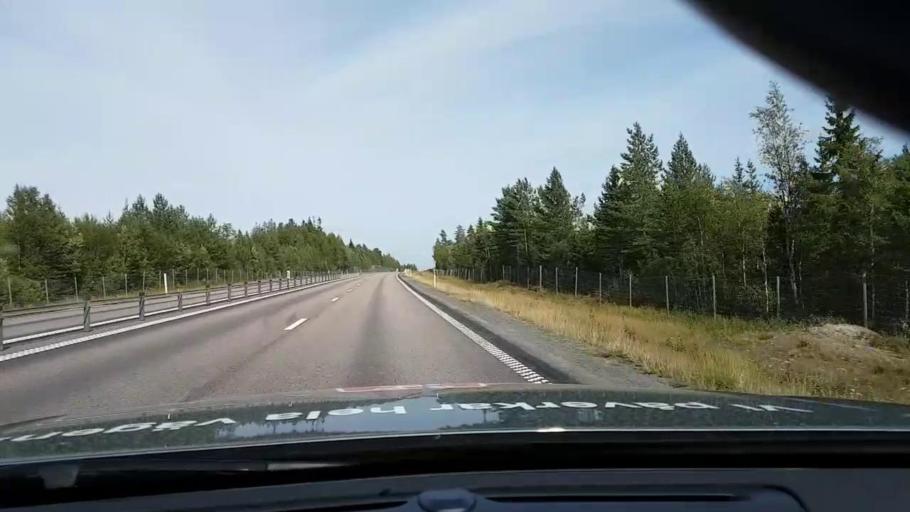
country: SE
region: Vaesternorrland
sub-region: OErnskoeldsviks Kommun
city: Husum
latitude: 63.4458
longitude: 19.2195
